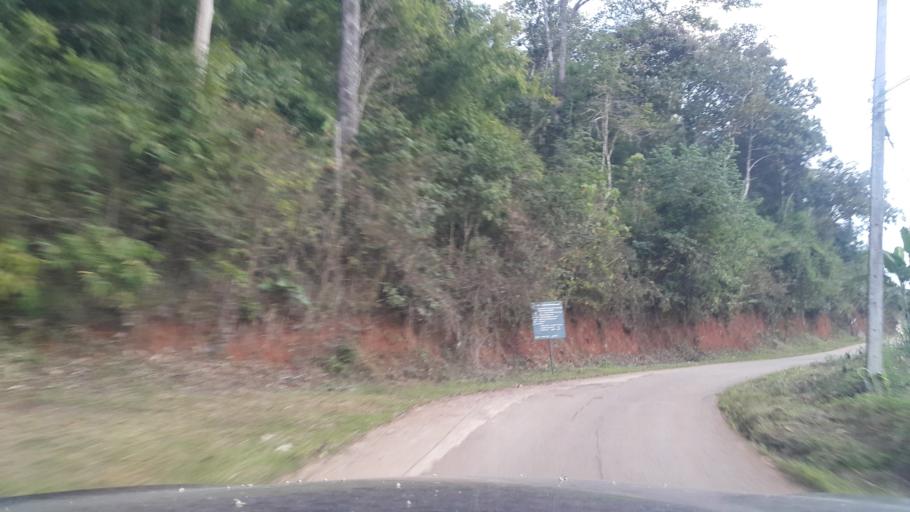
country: TH
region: Chiang Mai
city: Samoeng
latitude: 18.9759
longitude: 98.6788
